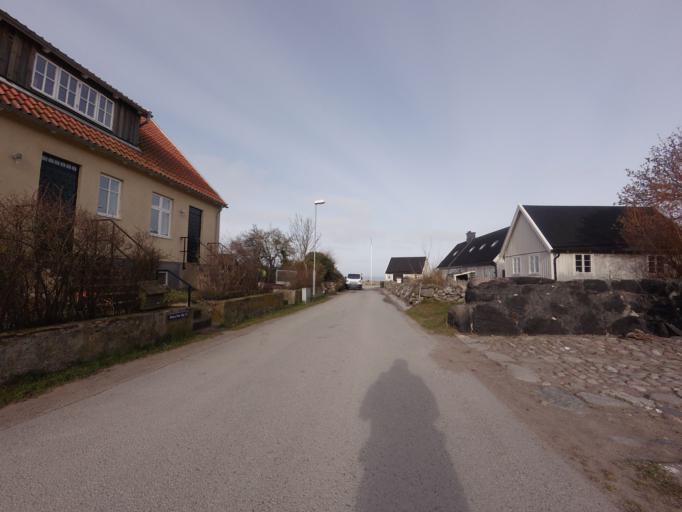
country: SE
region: Skane
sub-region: Hoganas Kommun
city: Hoganas
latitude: 56.2570
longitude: 12.5218
